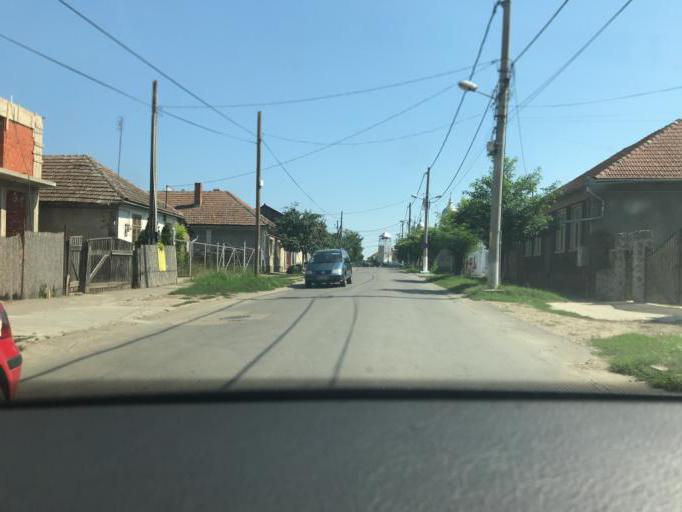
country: RO
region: Bihor
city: Margita
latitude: 47.3439
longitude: 22.3394
